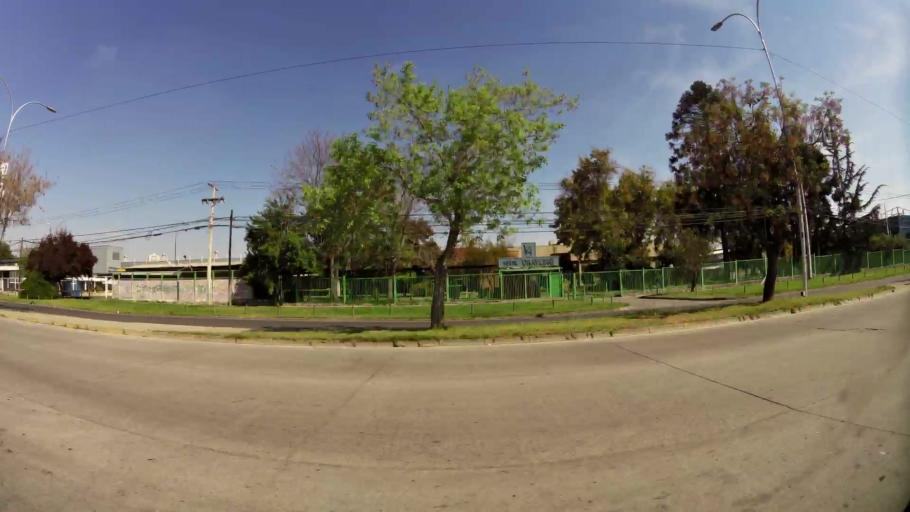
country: CL
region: Santiago Metropolitan
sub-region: Provincia de Santiago
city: Santiago
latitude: -33.4190
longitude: -70.6801
